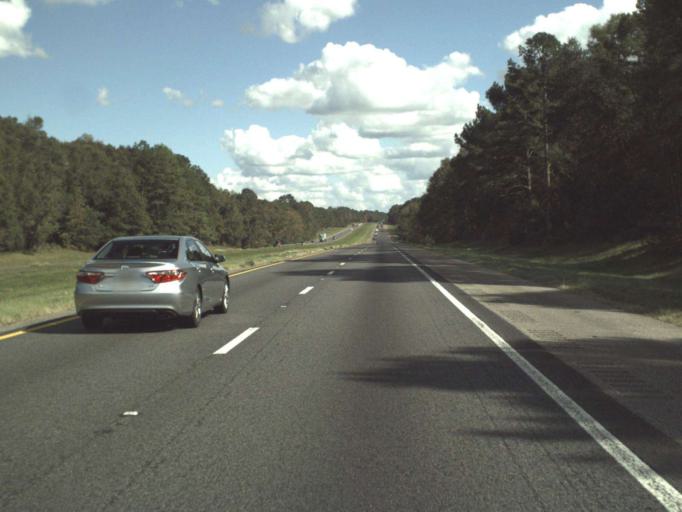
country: US
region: Florida
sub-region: Gadsden County
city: Gretna
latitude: 30.5676
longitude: -84.6641
